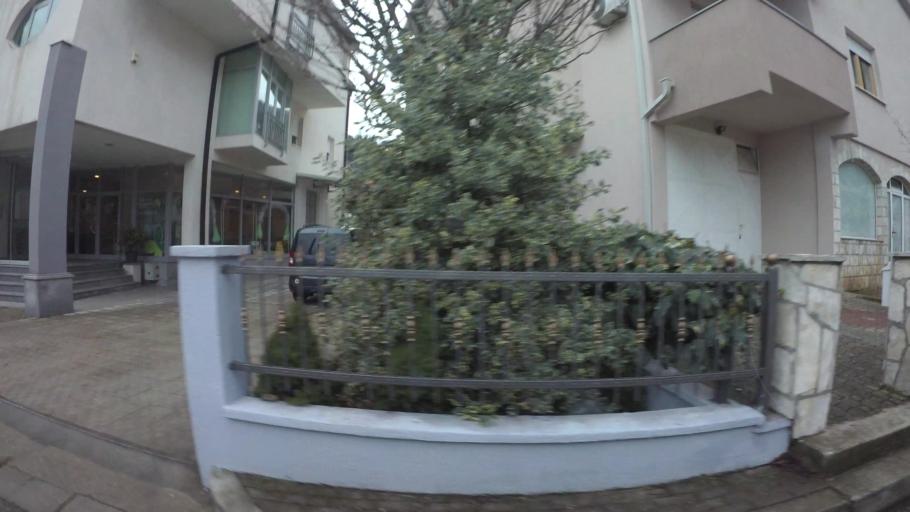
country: BA
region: Federation of Bosnia and Herzegovina
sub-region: Hercegovacko-Bosanski Kanton
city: Mostar
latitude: 43.3332
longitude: 17.7962
